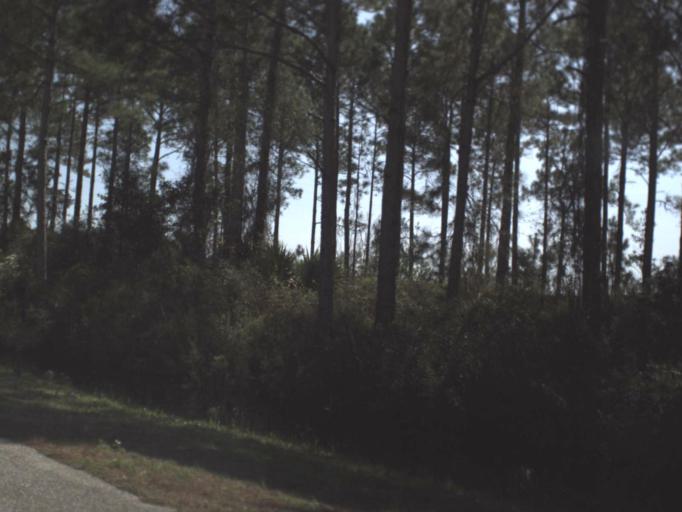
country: US
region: Florida
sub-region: Gulf County
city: Port Saint Joe
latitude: 29.7776
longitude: -85.2975
